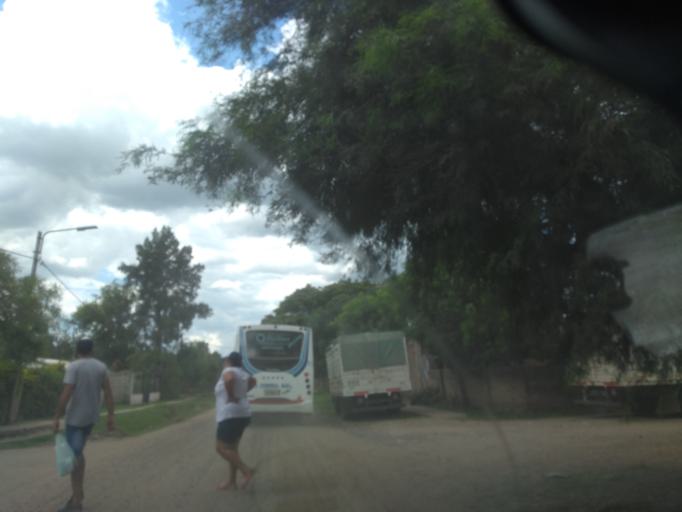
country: AR
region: Chaco
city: Fontana
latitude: -27.4050
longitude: -59.0442
